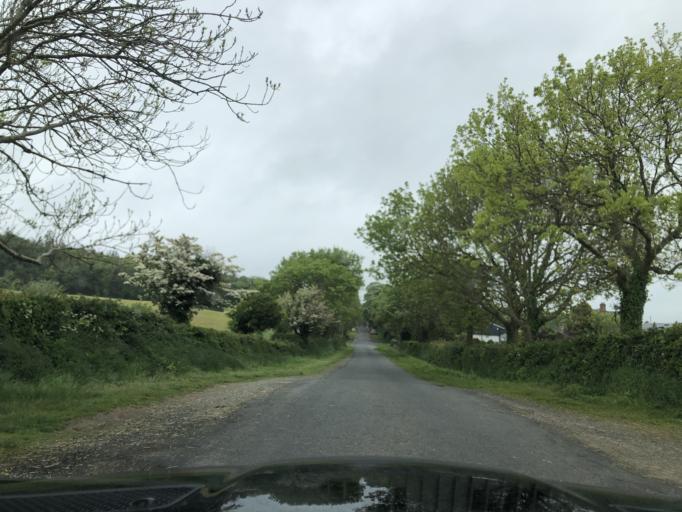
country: GB
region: Northern Ireland
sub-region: Down District
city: Portaferry
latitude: 54.3577
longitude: -5.5801
